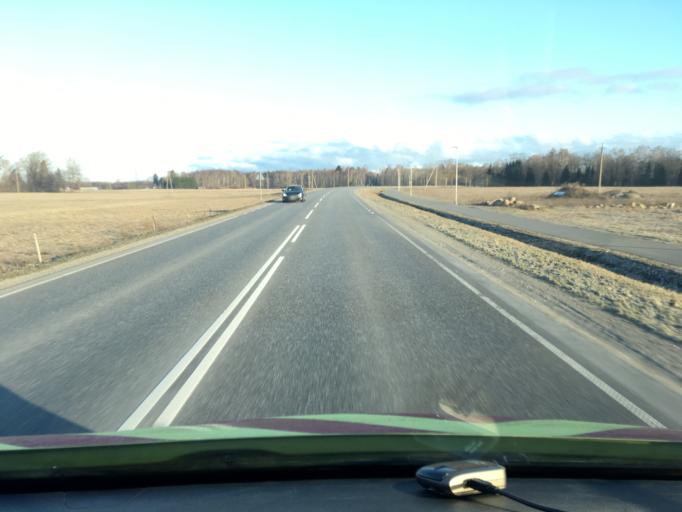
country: EE
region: Harju
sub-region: Saue vald
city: Laagri
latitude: 59.3685
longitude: 24.5886
